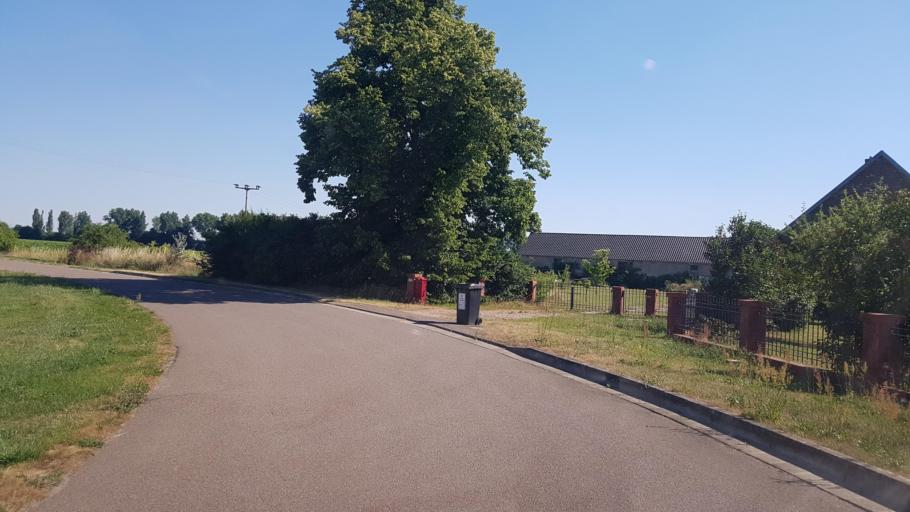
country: DE
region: Saxony-Anhalt
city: Elster
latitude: 51.7700
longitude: 12.8642
